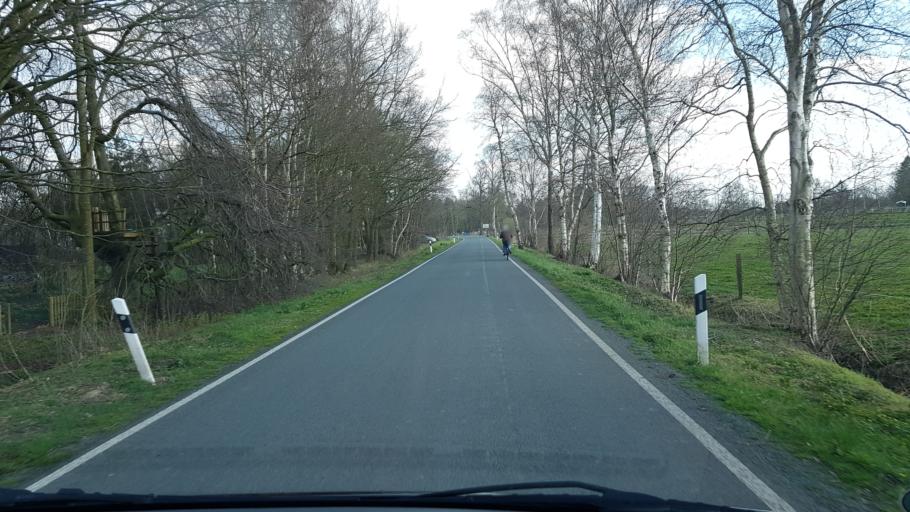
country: DE
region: Lower Saxony
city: Rastede
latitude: 53.3123
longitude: 8.2341
